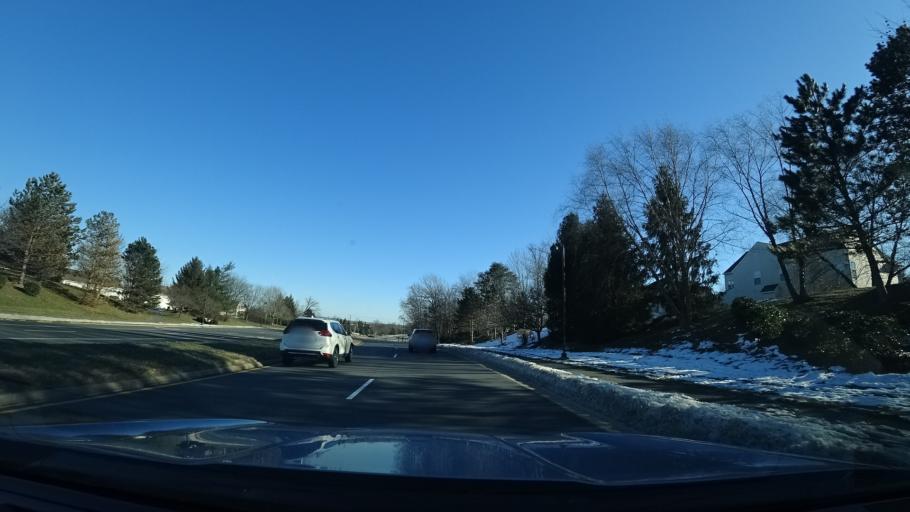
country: US
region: Virginia
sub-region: Loudoun County
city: Ashburn
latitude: 39.0517
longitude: -77.4864
